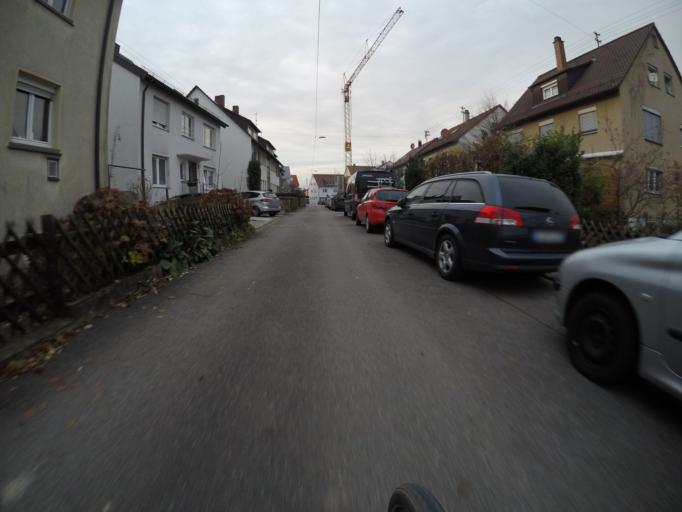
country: DE
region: Baden-Wuerttemberg
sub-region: Regierungsbezirk Stuttgart
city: Ostfildern
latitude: 48.7319
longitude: 9.2574
